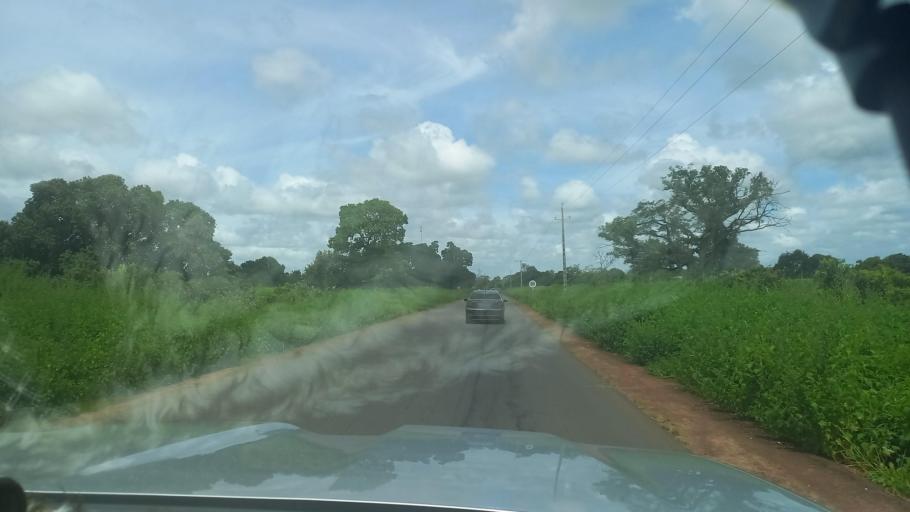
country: GM
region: Lower River
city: Kaiaf
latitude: 13.2016
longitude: -15.5508
